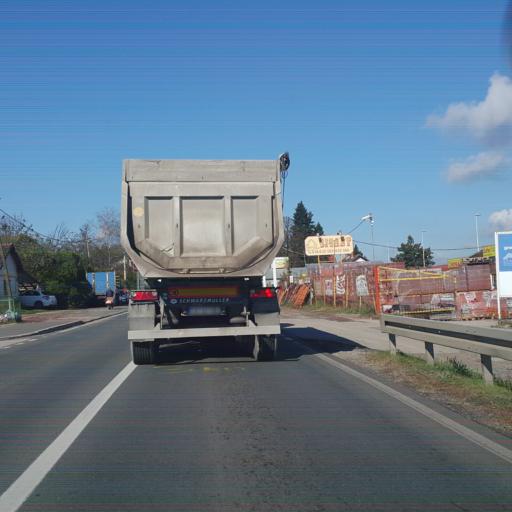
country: RS
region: Central Serbia
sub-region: Raski Okrug
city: Vrnjacka Banja
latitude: 43.6385
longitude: 20.9270
